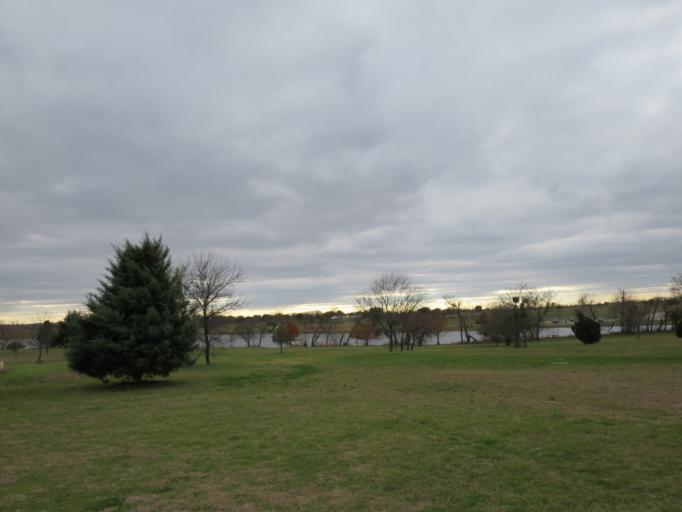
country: US
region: Texas
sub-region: Williamson County
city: Round Rock
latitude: 30.5403
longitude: -97.6249
